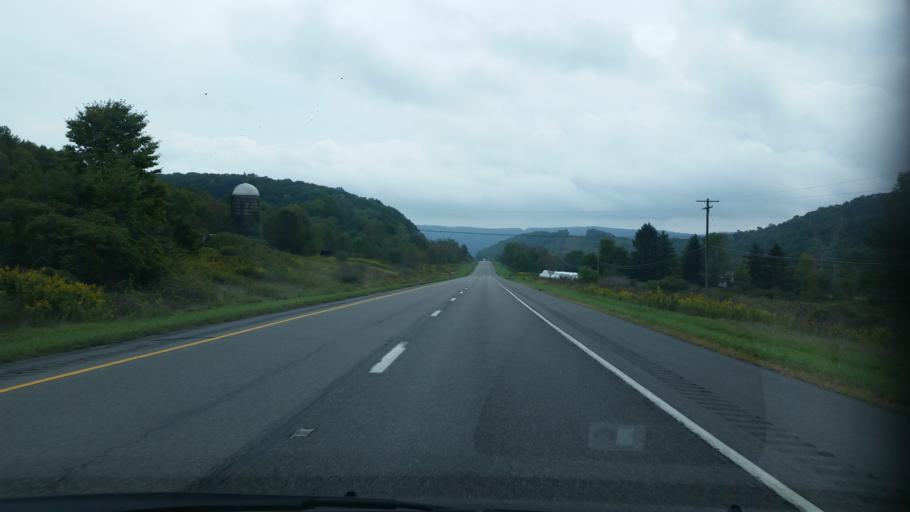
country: US
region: Pennsylvania
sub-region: Centre County
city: Stormstown
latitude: 40.8172
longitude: -78.0920
